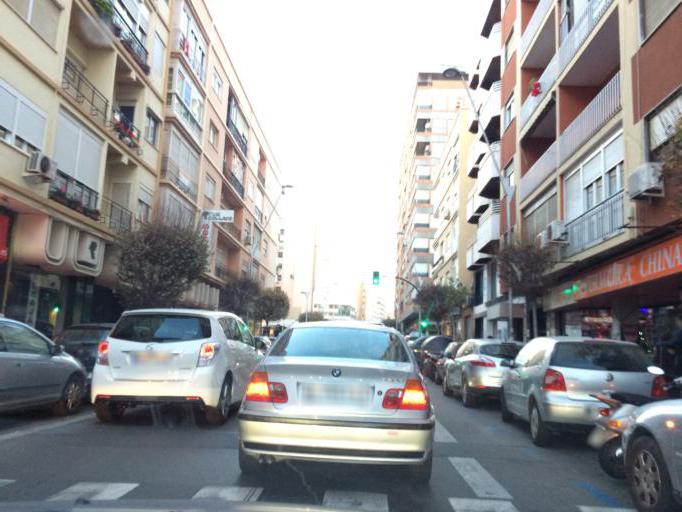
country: ES
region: Andalusia
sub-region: Provincia de Almeria
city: Almeria
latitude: 36.8382
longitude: -2.4576
